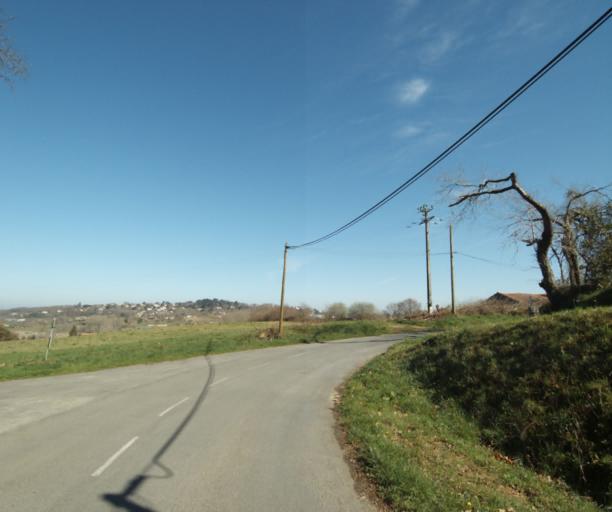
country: FR
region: Aquitaine
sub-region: Departement des Pyrenees-Atlantiques
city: Urrugne
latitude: 43.3653
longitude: -1.6842
